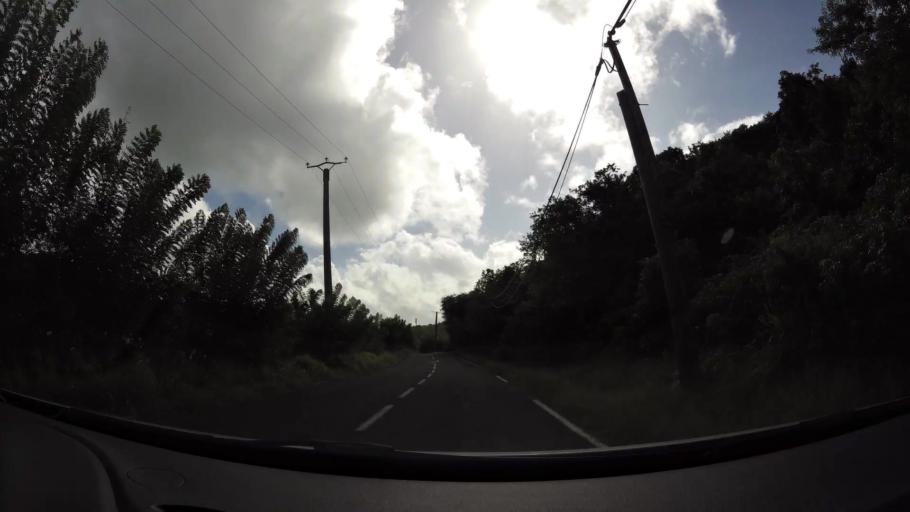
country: MQ
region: Martinique
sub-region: Martinique
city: Le Marin
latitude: 14.4271
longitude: -60.8759
